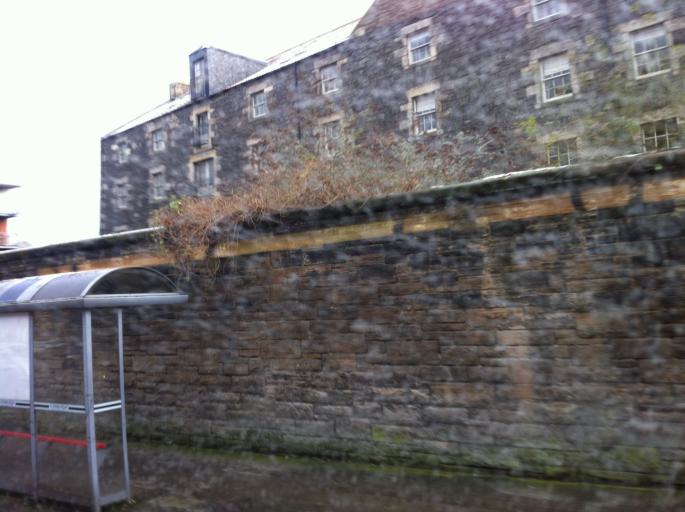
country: GB
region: Scotland
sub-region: West Lothian
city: Seafield
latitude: 55.9737
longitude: -3.1729
